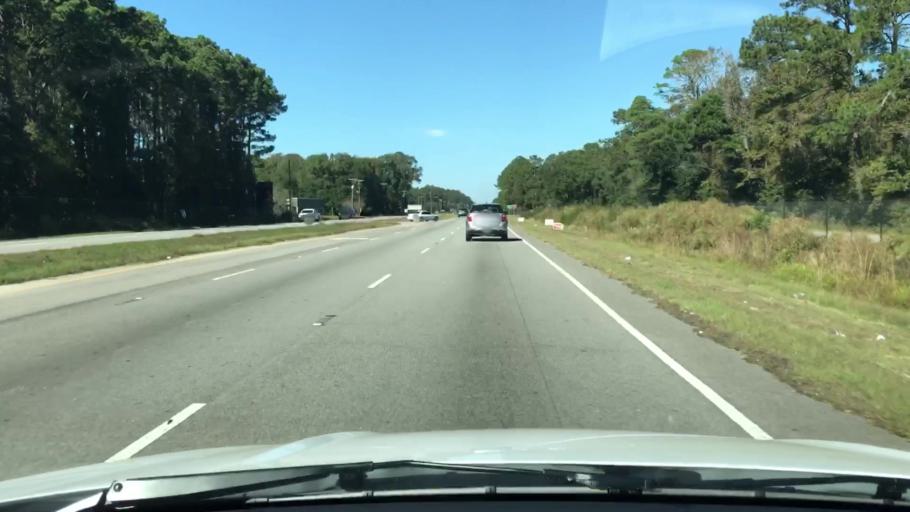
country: US
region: South Carolina
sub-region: Beaufort County
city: Burton
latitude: 32.4756
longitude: -80.7378
